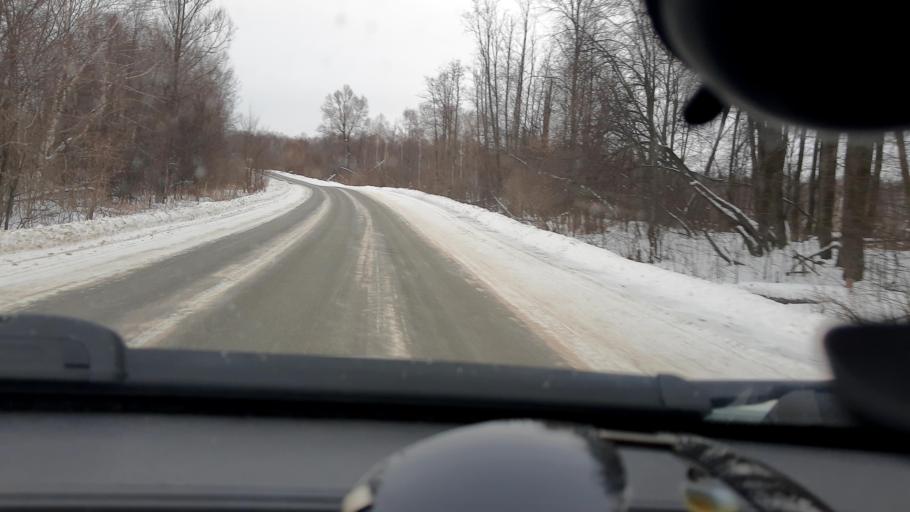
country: RU
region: Bashkortostan
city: Yazykovo
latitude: 55.0298
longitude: 56.2045
